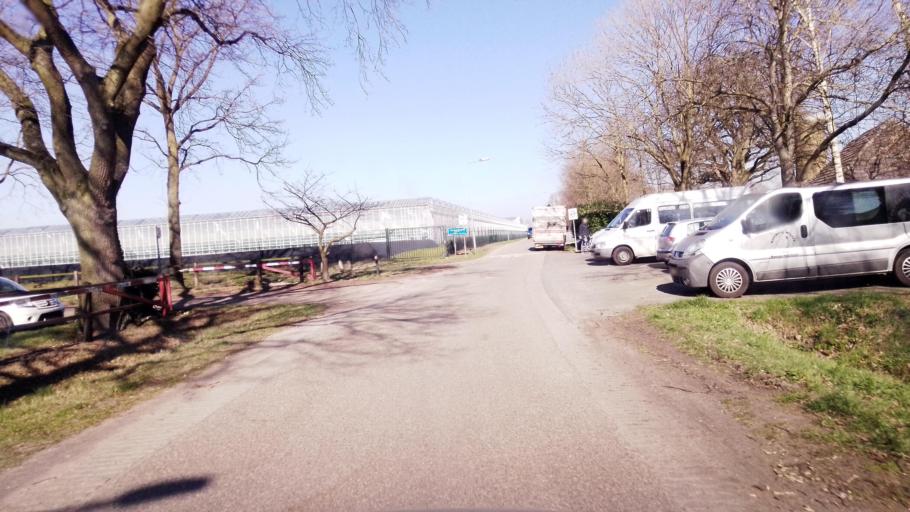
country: NL
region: Limburg
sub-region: Gemeente Peel en Maas
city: Maasbree
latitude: 51.4392
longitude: 6.0439
